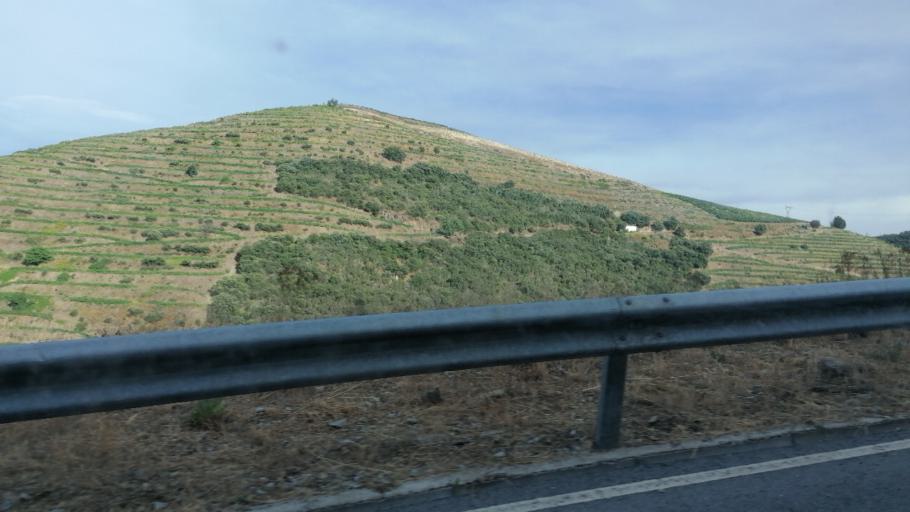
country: PT
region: Viseu
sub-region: Sao Joao da Pesqueira
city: Sao Joao da Pesqueira
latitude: 41.1173
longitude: -7.4547
